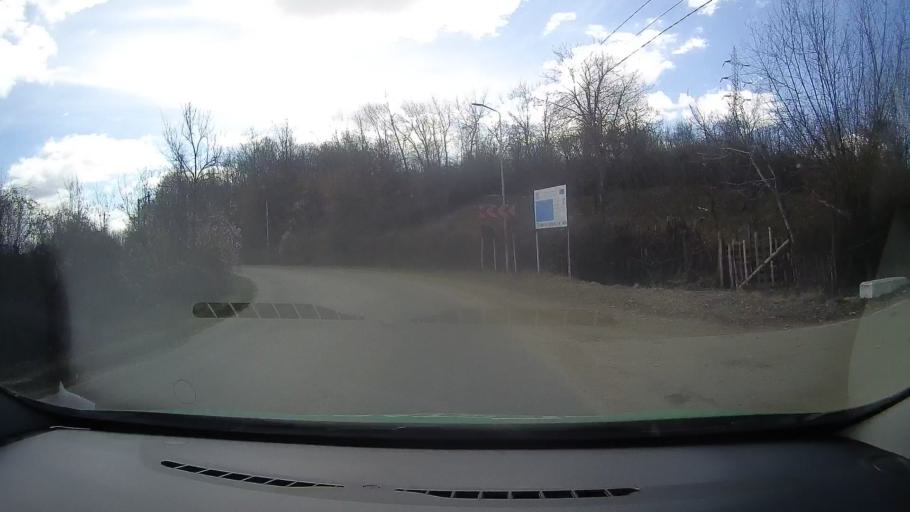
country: RO
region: Dambovita
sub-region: Comuna Sotanga
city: Teis
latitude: 44.9711
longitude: 25.3956
